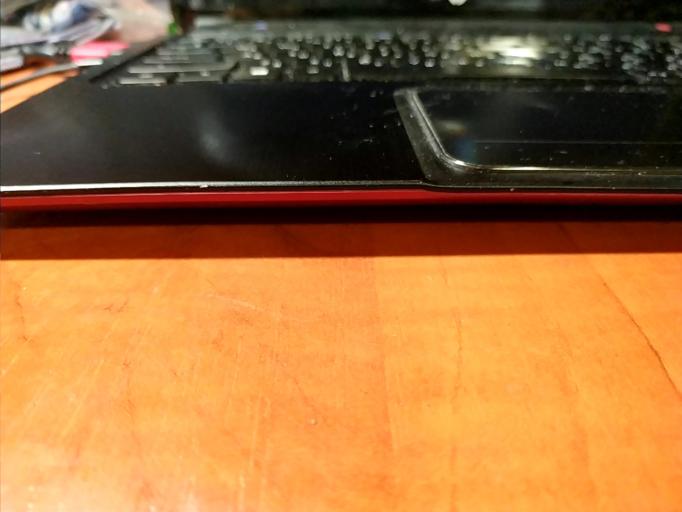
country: RU
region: Tverskaya
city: Ves'yegonsk
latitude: 58.7575
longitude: 37.5437
